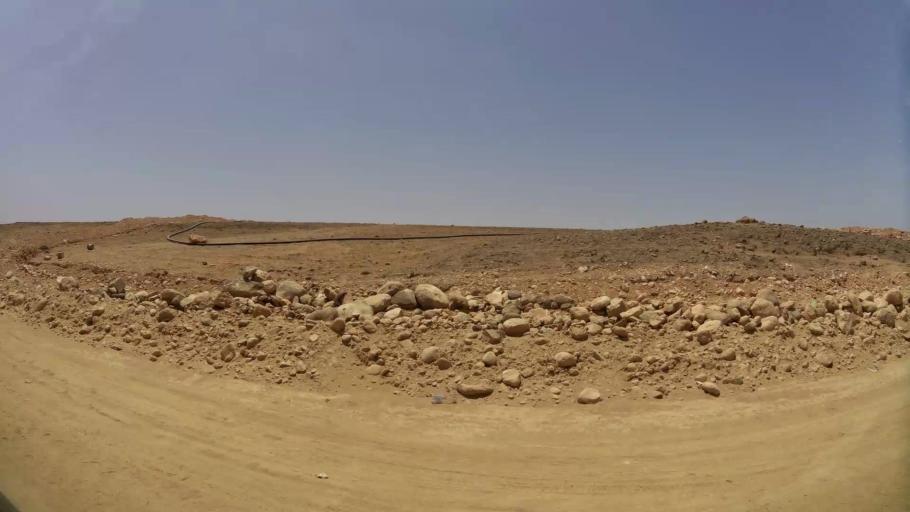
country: OM
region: Zufar
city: Salalah
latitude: 17.0810
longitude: 54.1867
